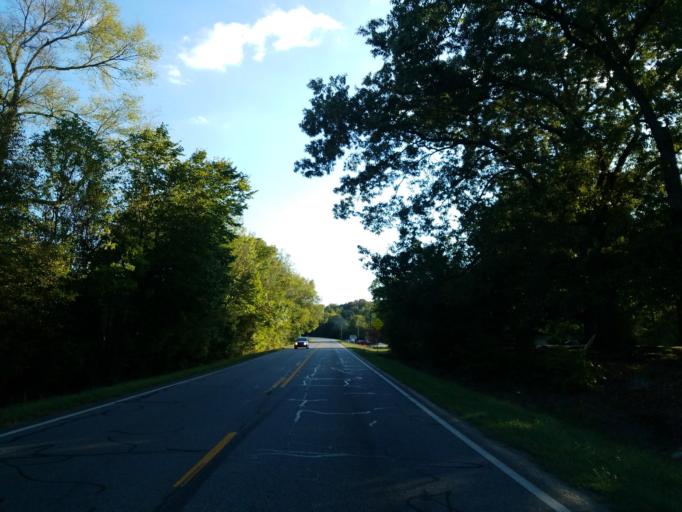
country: US
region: Georgia
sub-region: Murray County
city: Chatsworth
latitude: 34.5726
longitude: -84.7062
